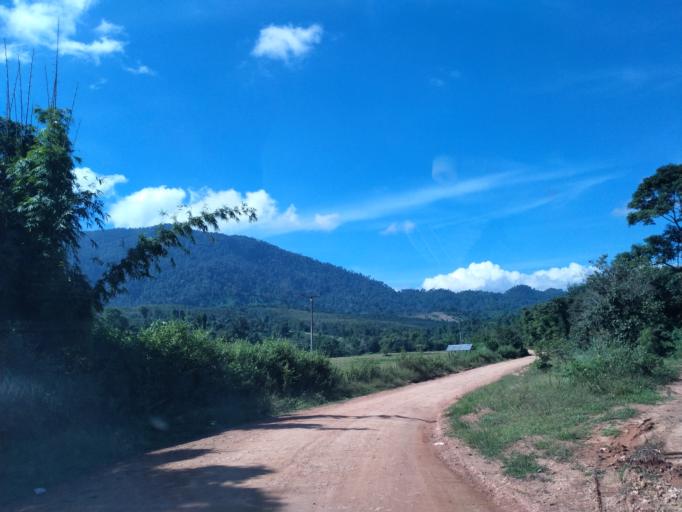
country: TH
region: Changwat Bueng Kan
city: Pak Khat
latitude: 18.6359
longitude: 103.0412
